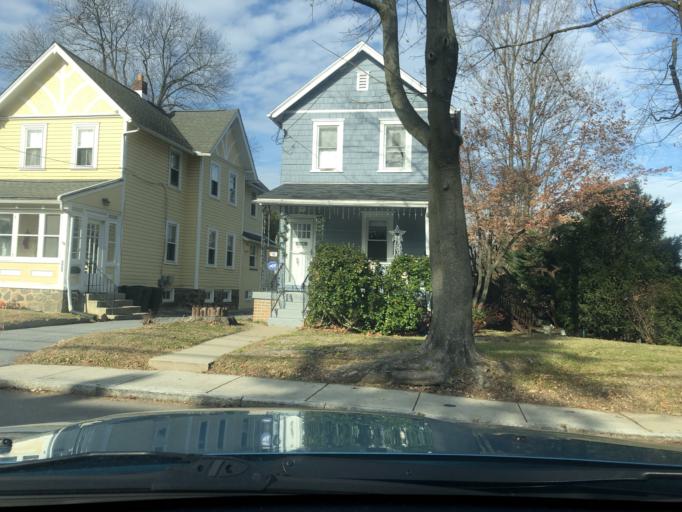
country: US
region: Pennsylvania
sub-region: Delaware County
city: Radnor
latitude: 40.0276
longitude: -75.3394
